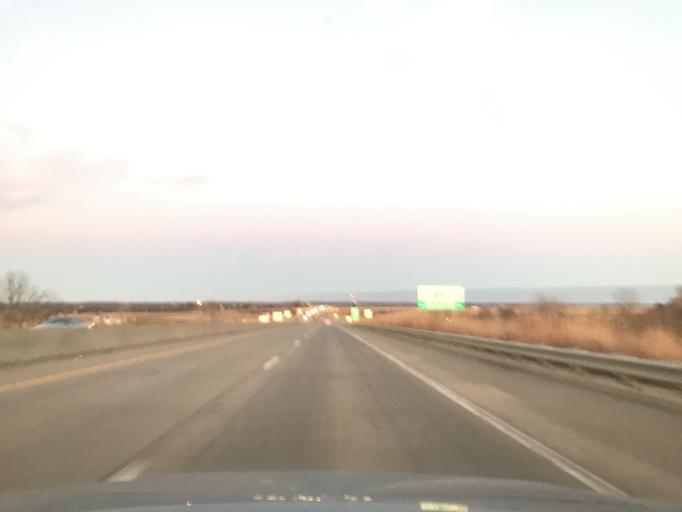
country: US
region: Missouri
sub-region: Marion County
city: Hannibal
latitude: 39.7242
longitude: -91.3464
